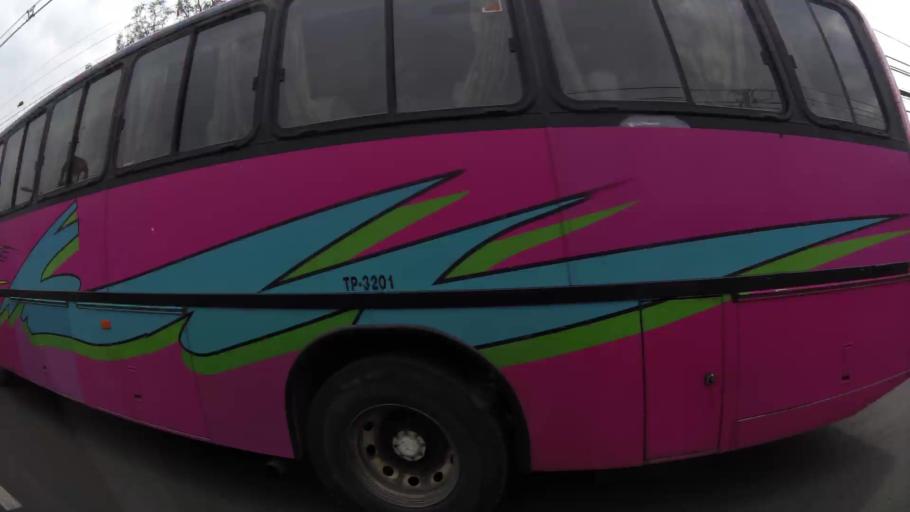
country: CL
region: Santiago Metropolitan
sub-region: Provincia de Chacabuco
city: Chicureo Abajo
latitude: -33.2055
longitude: -70.6768
